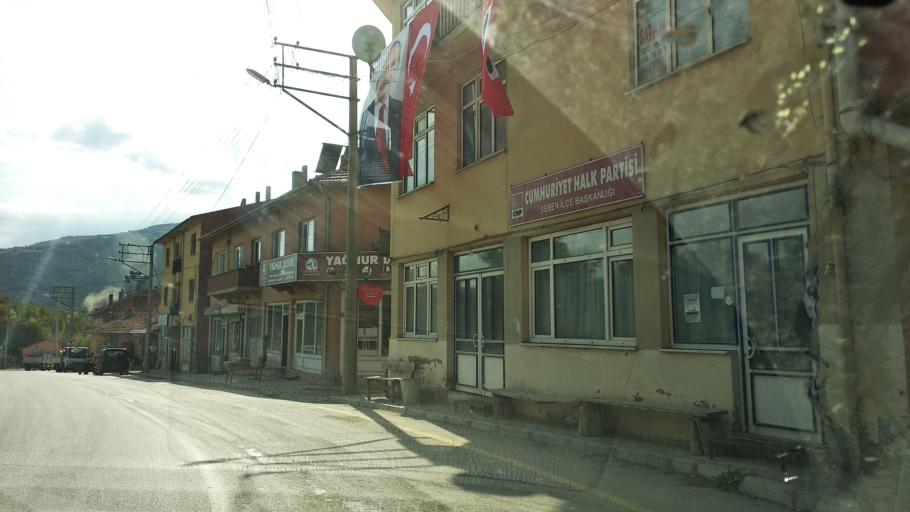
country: TR
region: Bolu
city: Seben
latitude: 40.4082
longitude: 31.5724
